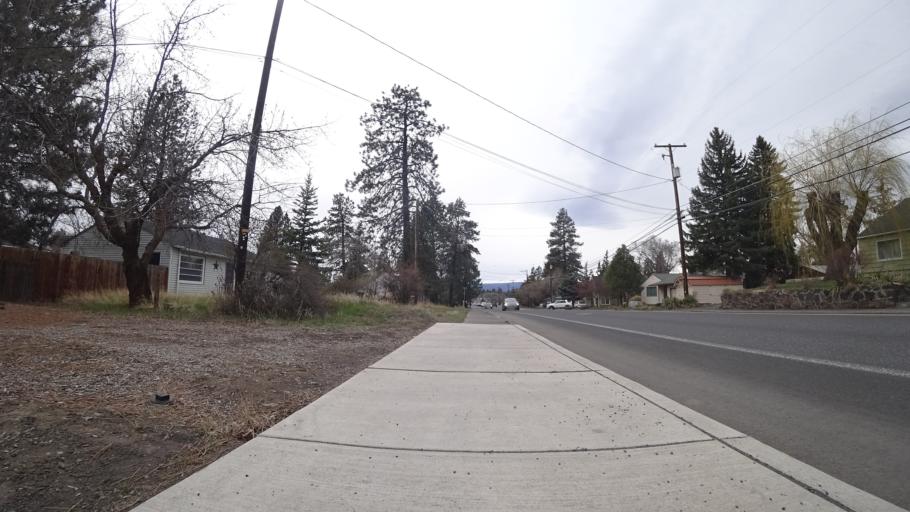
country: US
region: Oregon
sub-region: Deschutes County
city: Bend
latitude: 44.0559
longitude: -121.2982
